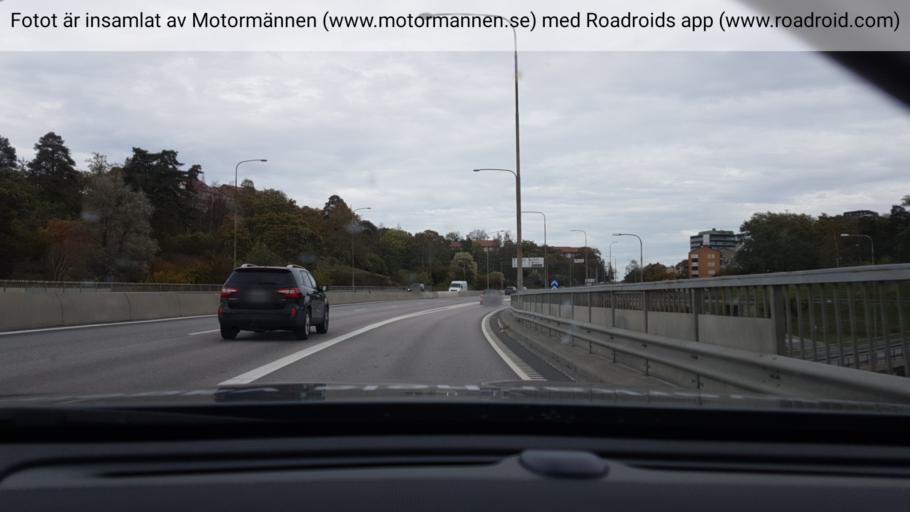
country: SE
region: Stockholm
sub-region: Lidingo
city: Lidingoe
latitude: 59.3624
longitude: 18.1160
